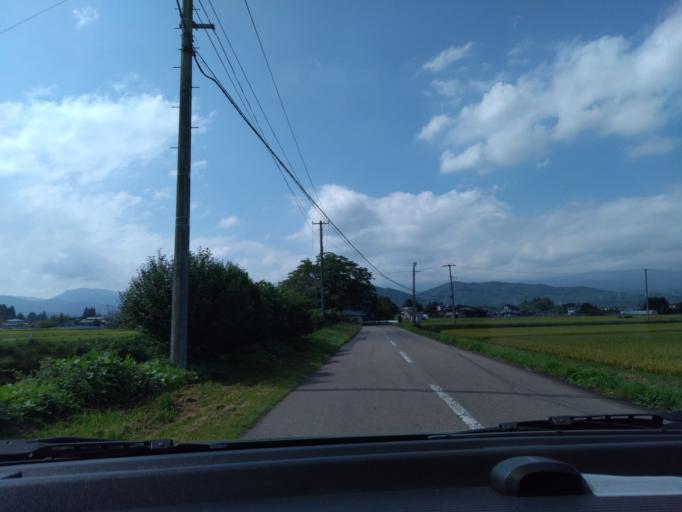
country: JP
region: Iwate
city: Shizukuishi
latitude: 39.6858
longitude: 140.9492
